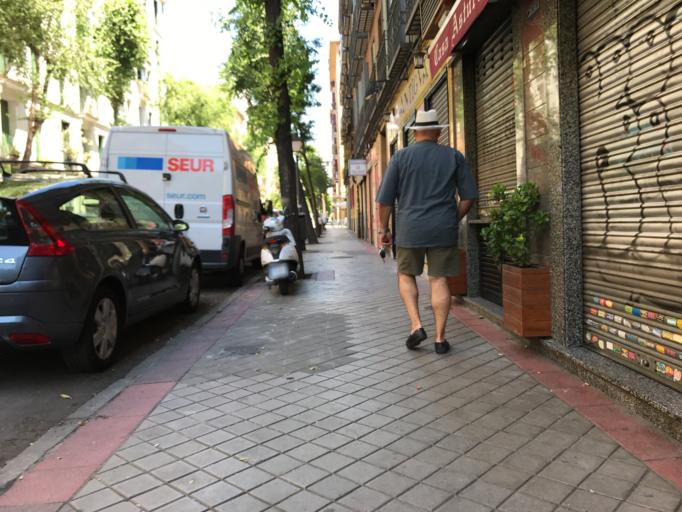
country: ES
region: Madrid
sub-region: Provincia de Madrid
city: Arganzuela
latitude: 40.4041
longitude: -3.6929
